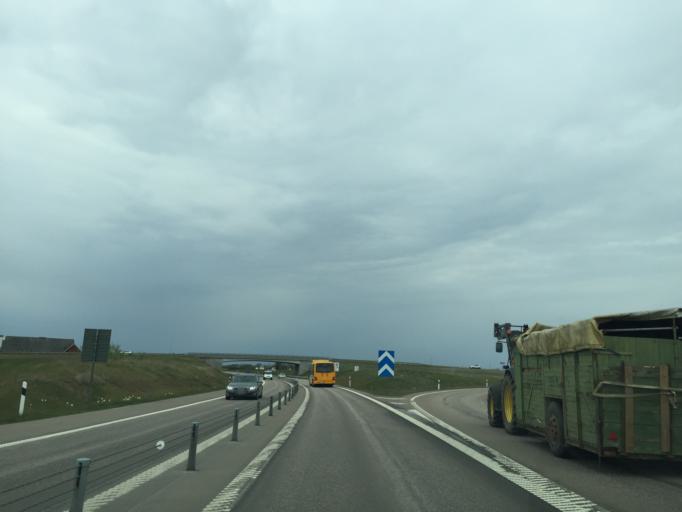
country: SE
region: Skane
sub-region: Hoganas Kommun
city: Hoganas
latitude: 56.1627
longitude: 12.5879
